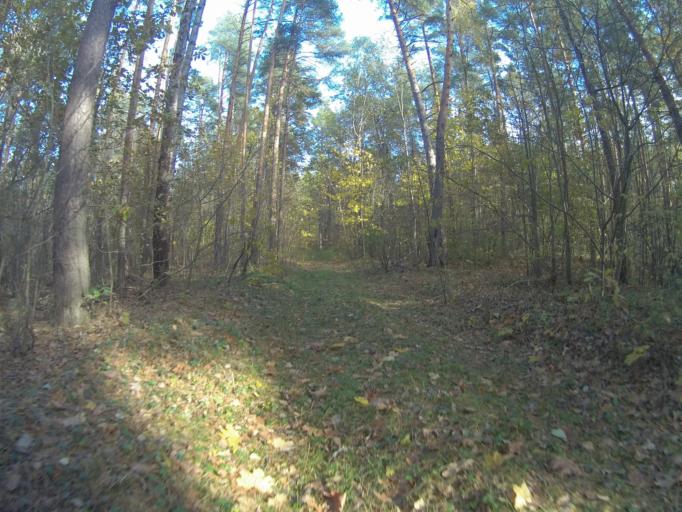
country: RU
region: Vladimir
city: Bogolyubovo
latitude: 56.1556
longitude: 40.5463
